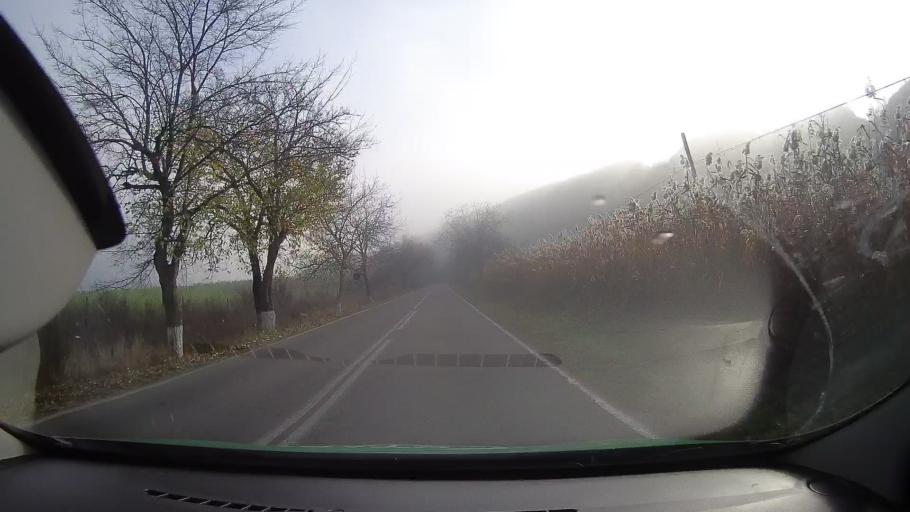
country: RO
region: Tulcea
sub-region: Comuna Nufaru
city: Nufaru
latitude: 45.1466
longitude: 28.9069
